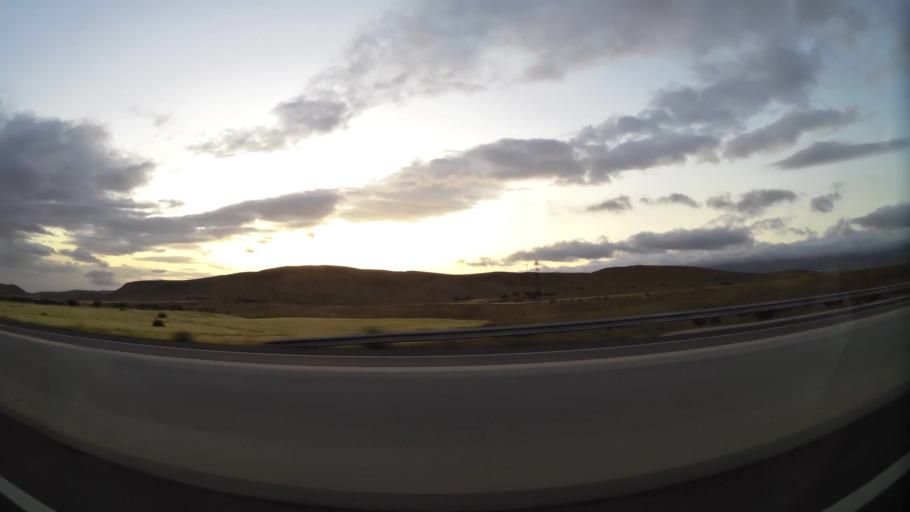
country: MA
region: Oriental
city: El Aioun
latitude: 34.6131
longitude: -2.5552
